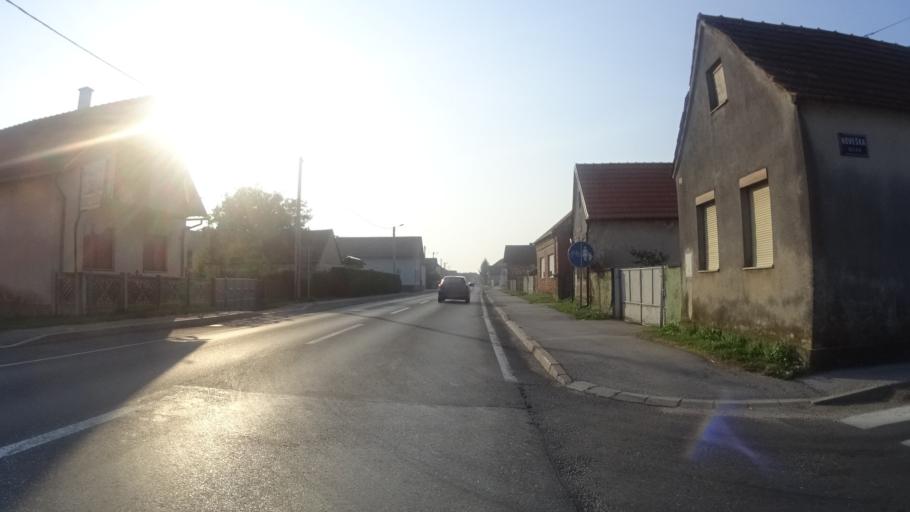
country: HR
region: Varazdinska
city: Petrijanec
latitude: 46.3416
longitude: 16.2429
